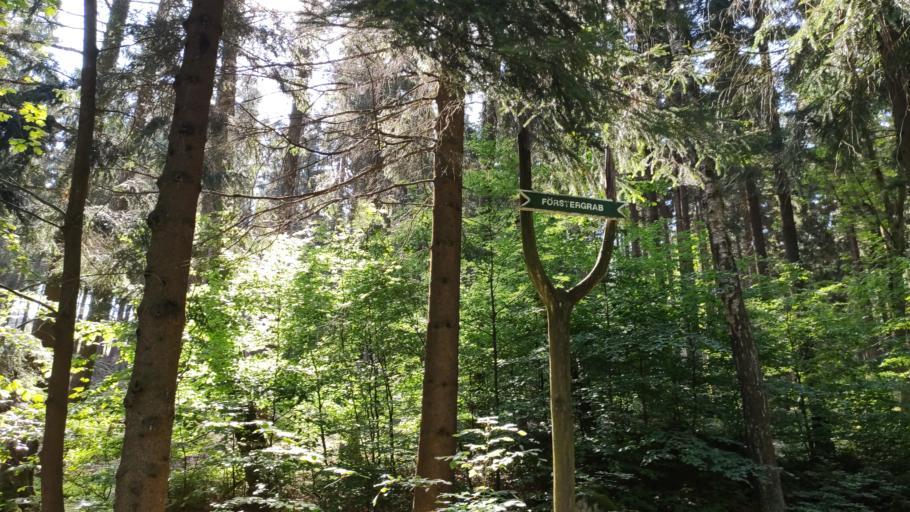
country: DE
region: Thuringia
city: Wurzbach
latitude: 50.4756
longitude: 11.4760
